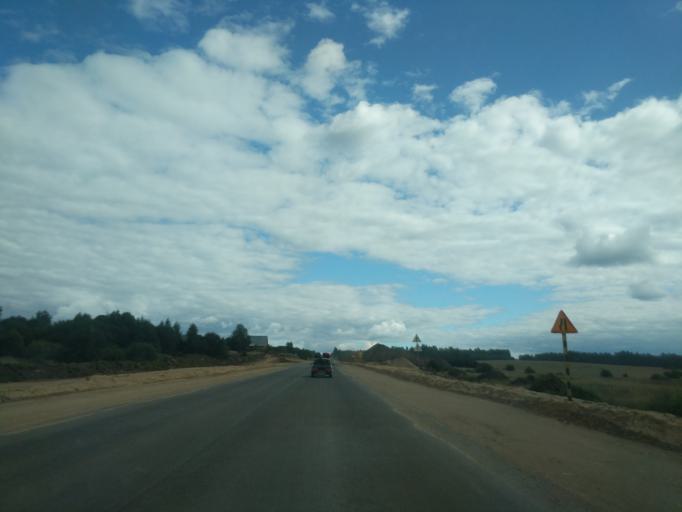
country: RU
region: Kostroma
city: Sudislavl'
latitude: 57.8752
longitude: 41.7338
